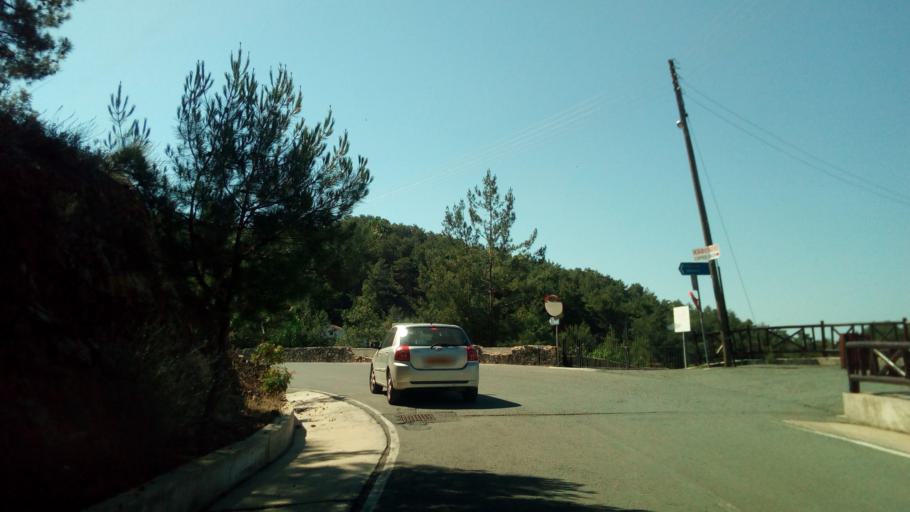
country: CY
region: Lefkosia
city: Lythrodontas
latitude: 34.8923
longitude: 33.2308
